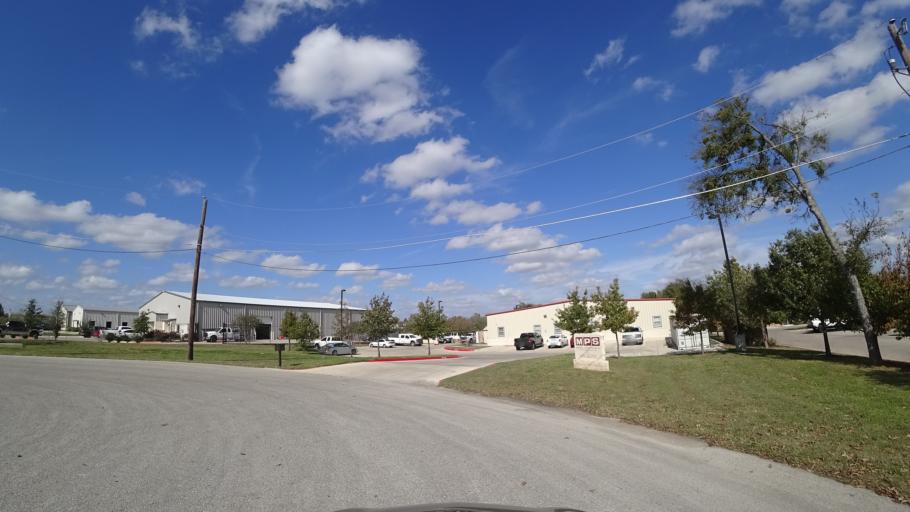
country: US
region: Texas
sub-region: Travis County
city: Windemere
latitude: 30.4643
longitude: -97.6570
